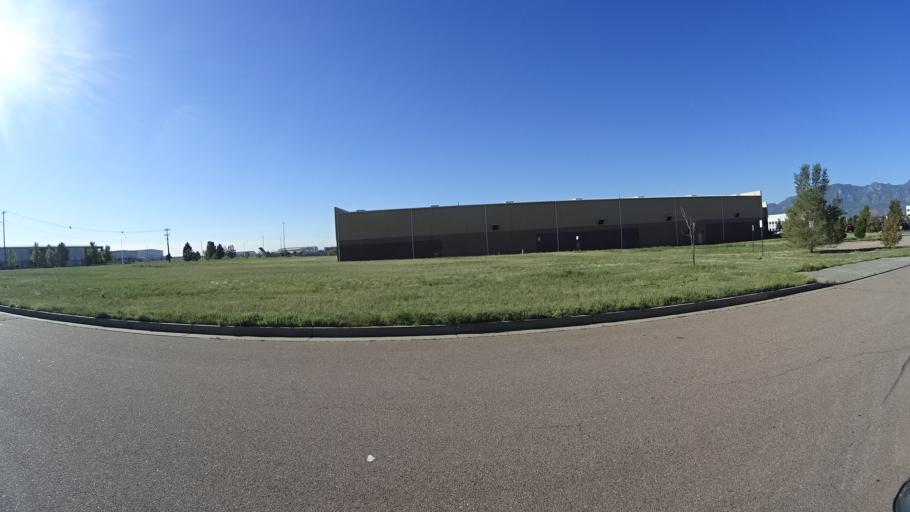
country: US
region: Colorado
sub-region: El Paso County
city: Cimarron Hills
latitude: 38.8184
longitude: -104.7239
